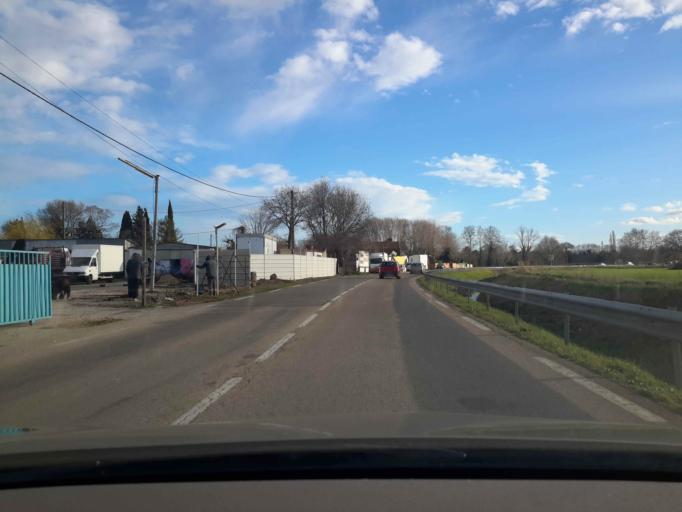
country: FR
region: Languedoc-Roussillon
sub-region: Departement du Gard
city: Caissargues
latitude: 43.7954
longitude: 4.3522
